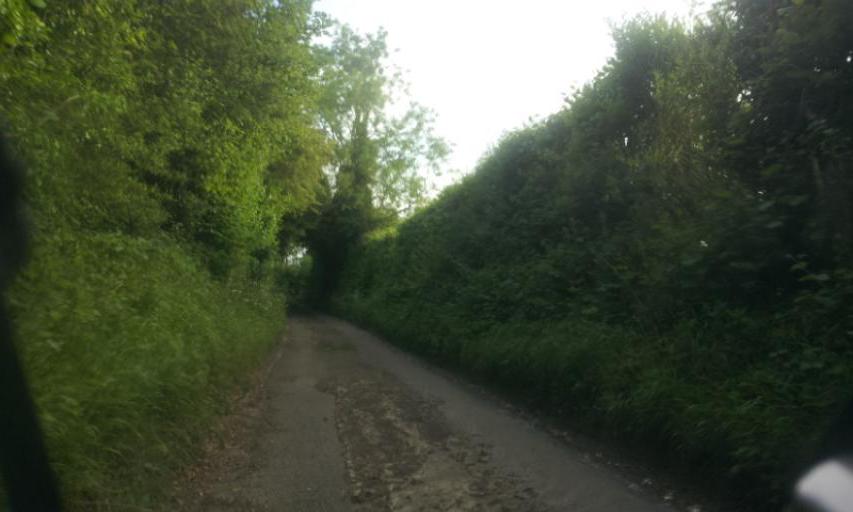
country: GB
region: England
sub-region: Kent
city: Lenham
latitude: 51.2482
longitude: 0.7057
